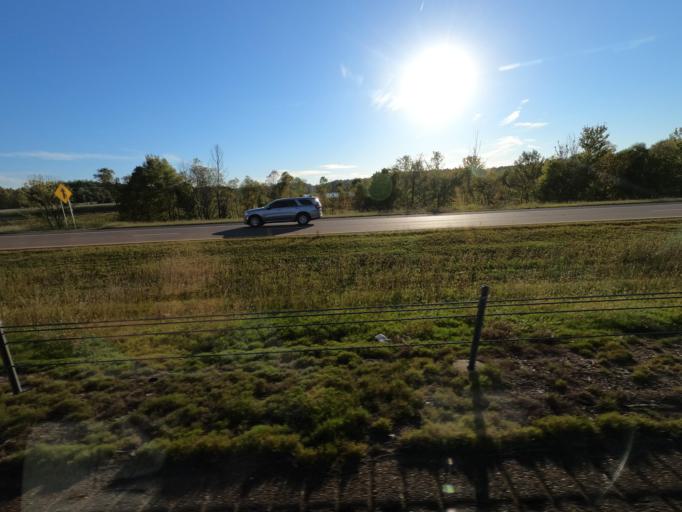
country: US
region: Tennessee
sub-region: Shelby County
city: Arlington
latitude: 35.2908
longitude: -89.6884
